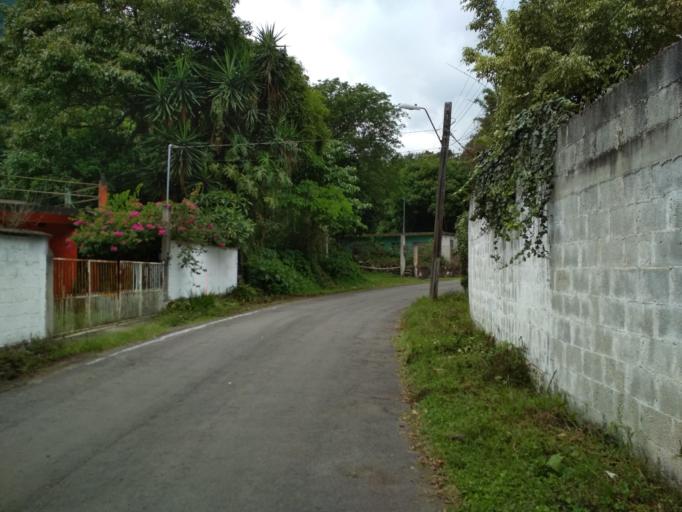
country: MX
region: Veracruz
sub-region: Jilotepec
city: El Pueblito (Garbanzal)
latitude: 19.6178
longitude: -96.9278
